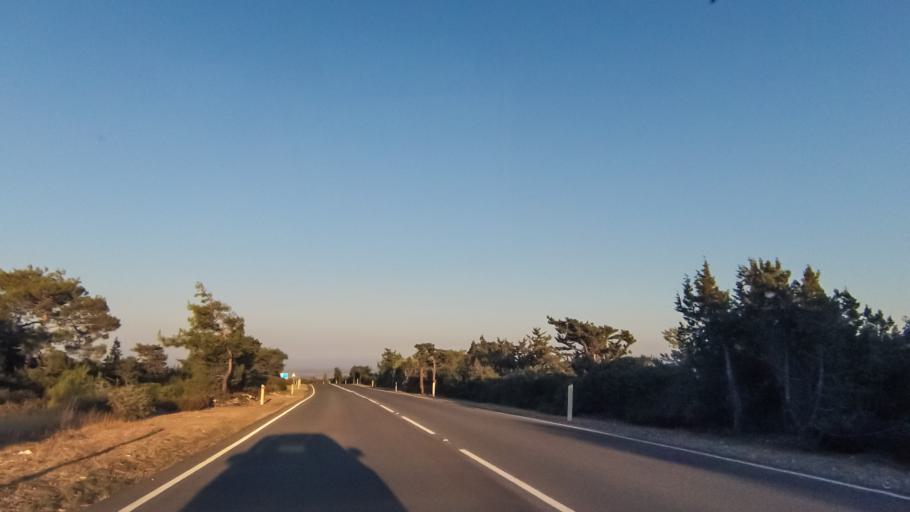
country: CY
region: Limassol
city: Sotira
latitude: 34.6712
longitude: 32.8586
